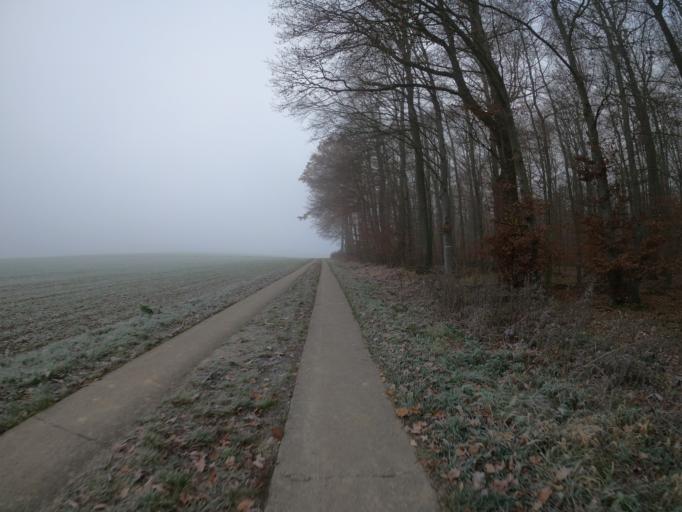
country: DE
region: Baden-Wuerttemberg
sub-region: Tuebingen Region
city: Beimerstetten
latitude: 48.4887
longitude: 9.9705
